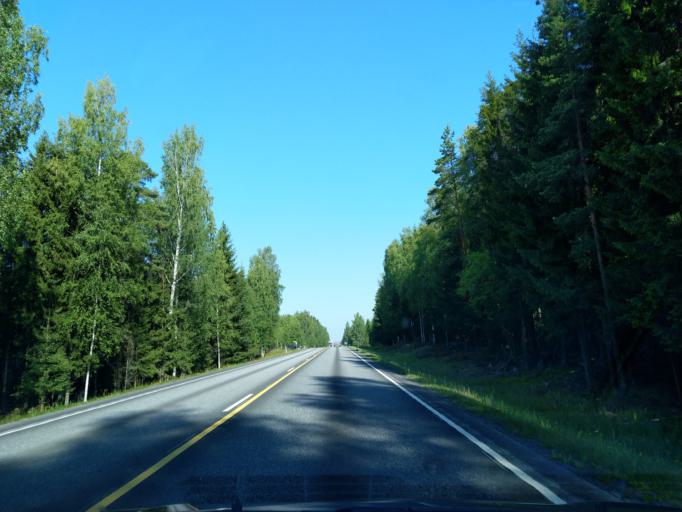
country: FI
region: Varsinais-Suomi
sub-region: Loimaa
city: Alastaro
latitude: 61.0745
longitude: 22.9147
